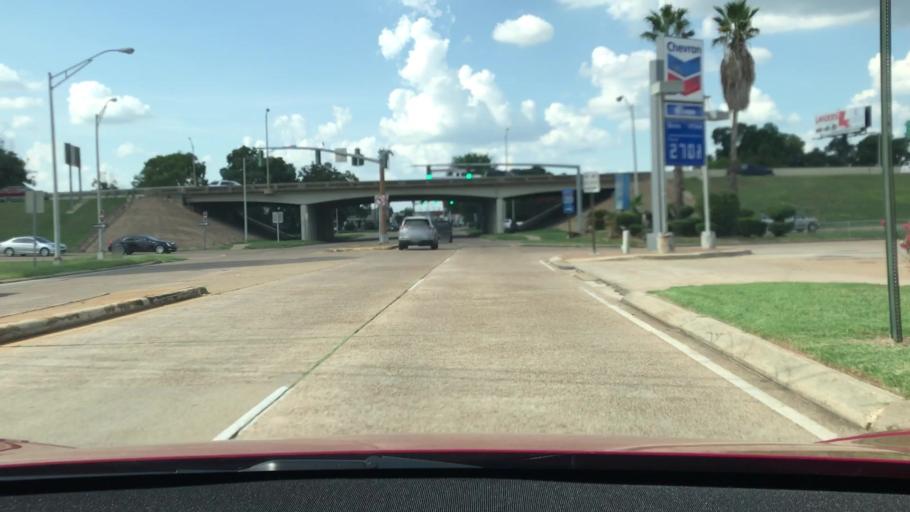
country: US
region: Louisiana
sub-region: Bossier Parish
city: Bossier City
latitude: 32.5129
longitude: -93.7266
